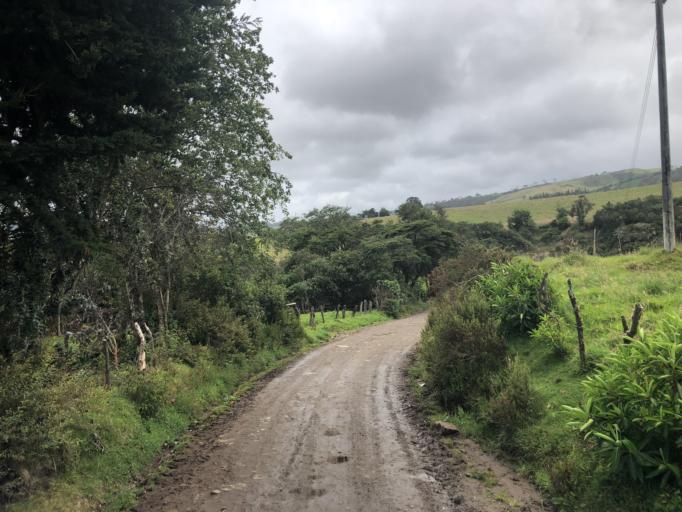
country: CO
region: Cauca
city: Totoro
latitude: 2.5033
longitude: -76.2769
